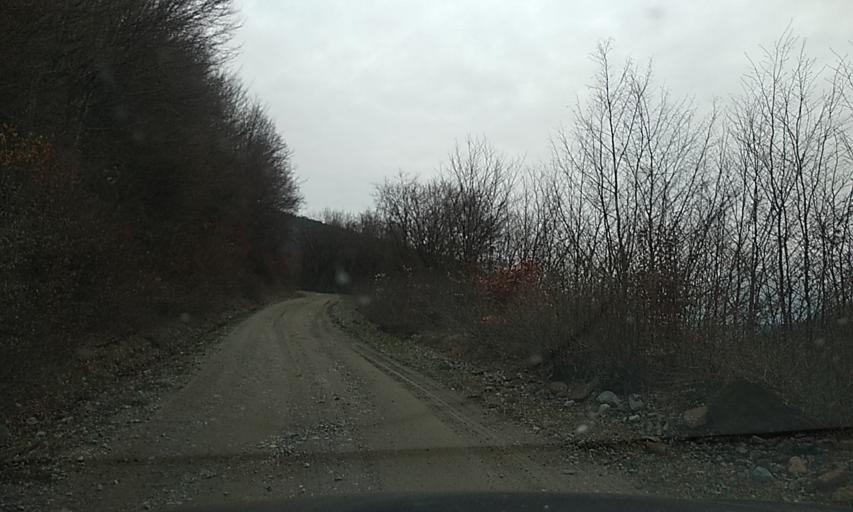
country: MK
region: Kriva Palanka
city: Kriva Palanka
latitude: 42.3405
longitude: 22.3590
